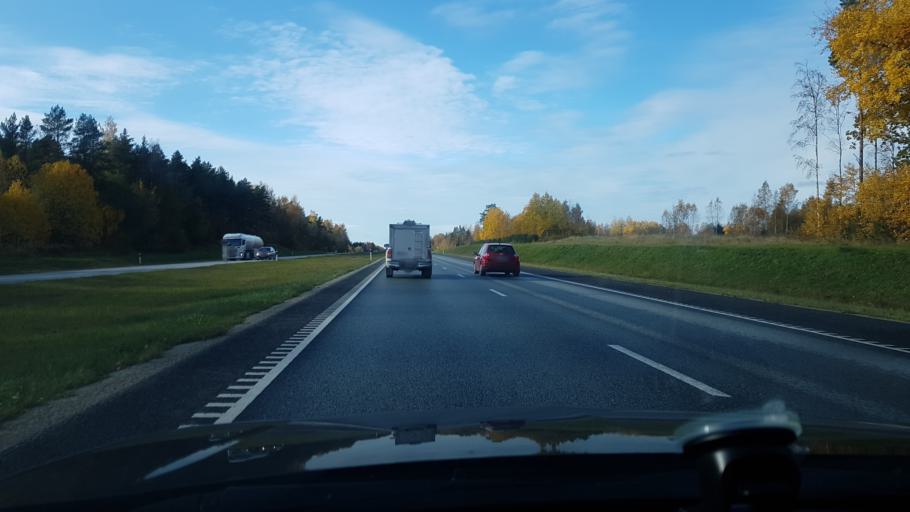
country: EE
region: Harju
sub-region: Raasiku vald
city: Raasiku
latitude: 59.4369
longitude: 25.2278
